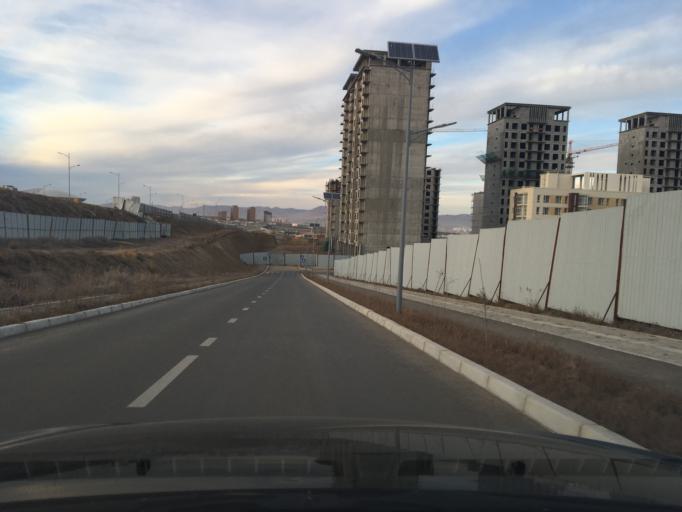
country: MN
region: Ulaanbaatar
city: Ulaanbaatar
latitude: 47.8470
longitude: 106.7910
